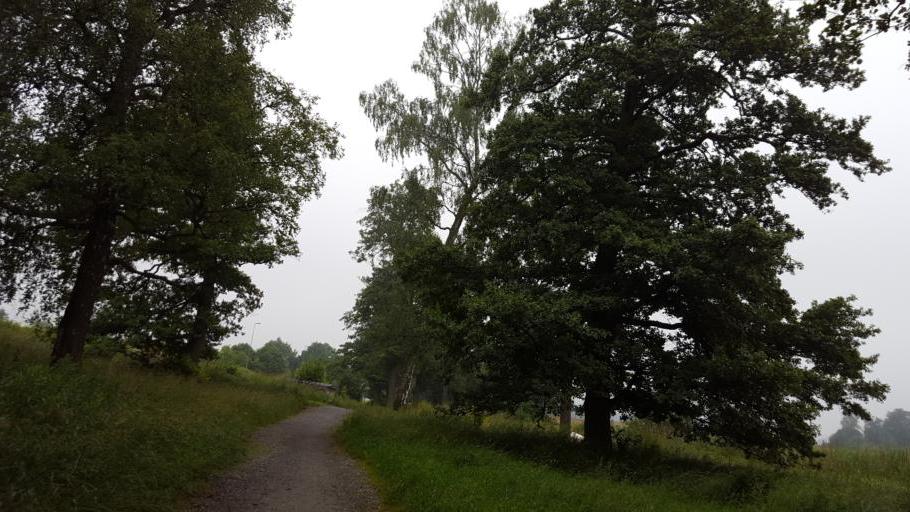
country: SE
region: Stockholm
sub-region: Upplands Vasby Kommun
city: Upplands Vaesby
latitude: 59.5081
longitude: 17.8827
